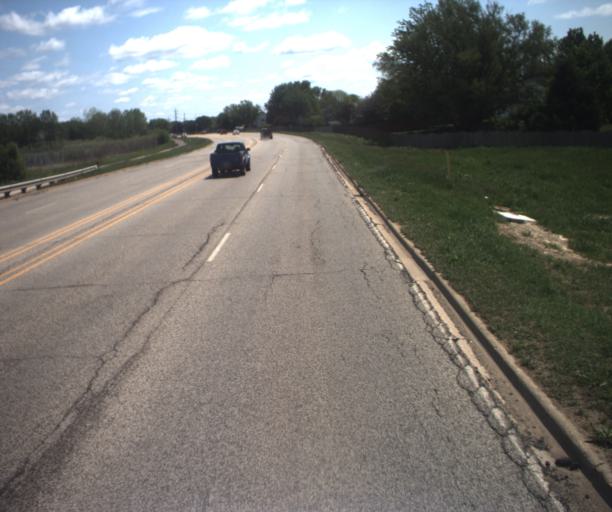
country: US
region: Illinois
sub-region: Kane County
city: Batavia
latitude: 41.8642
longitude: -88.3332
